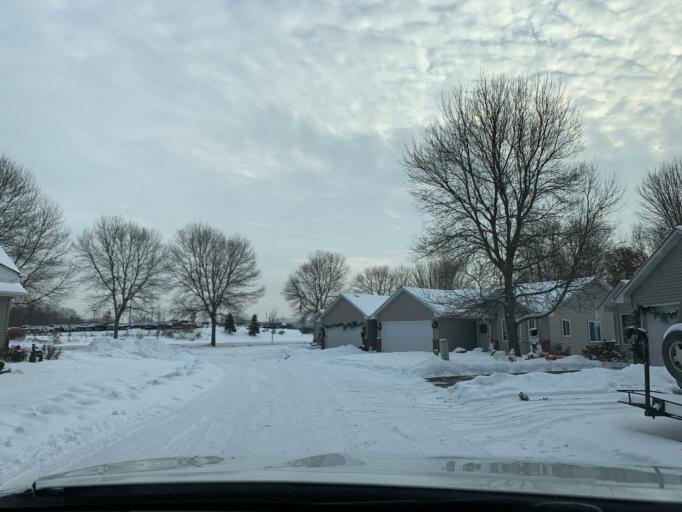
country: US
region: Minnesota
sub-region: Anoka County
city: Coon Rapids
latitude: 45.1617
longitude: -93.2896
